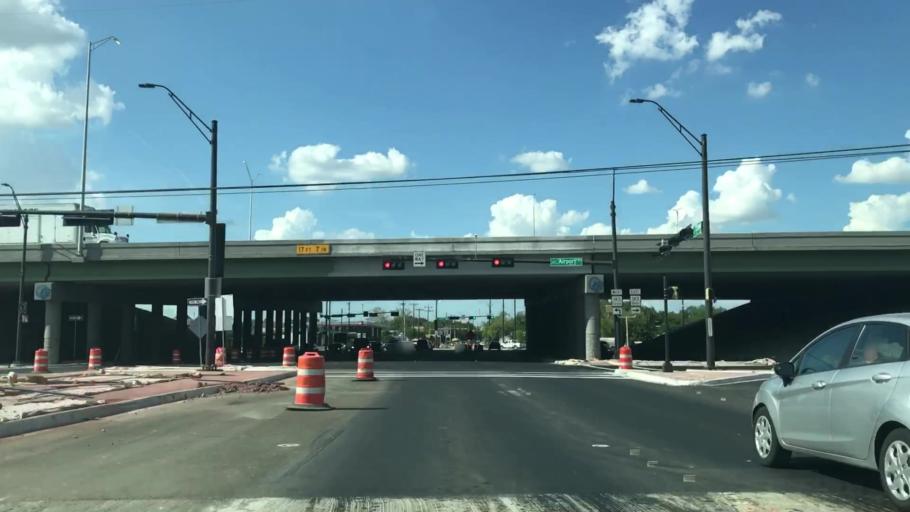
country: US
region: Texas
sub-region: Dallas County
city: Irving
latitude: 32.8363
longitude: -96.9511
